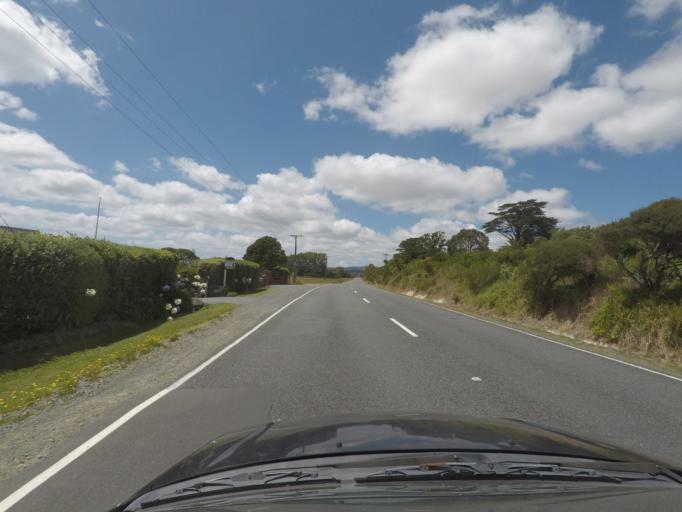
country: NZ
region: Northland
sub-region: Whangarei
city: Ruakaka
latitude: -35.9959
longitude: 174.4723
